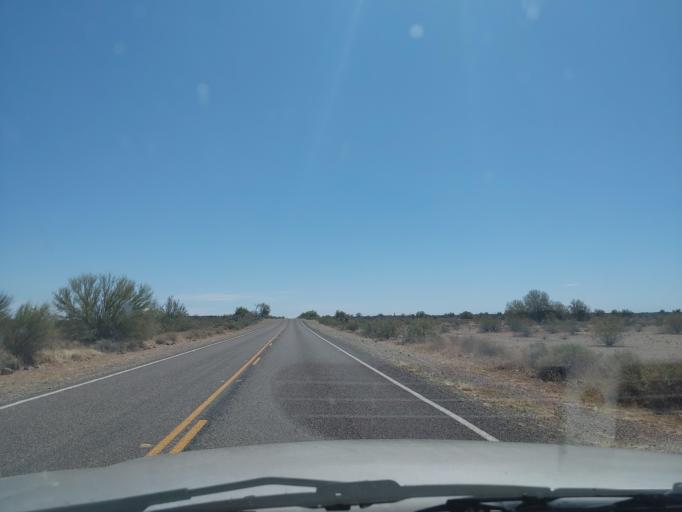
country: US
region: Arizona
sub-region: Maricopa County
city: Gila Bend
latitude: 32.9103
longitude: -113.2707
